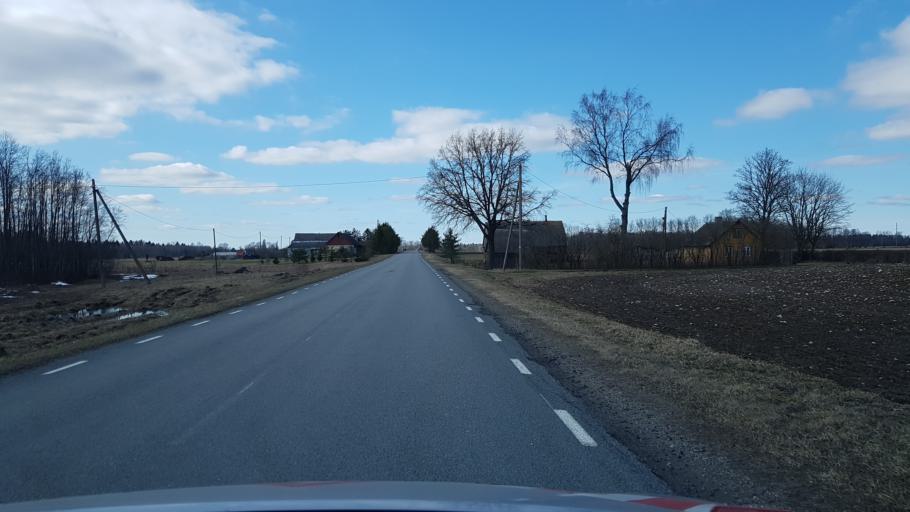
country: EE
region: Laeaene-Virumaa
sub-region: Tamsalu vald
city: Tamsalu
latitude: 59.1814
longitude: 26.0489
